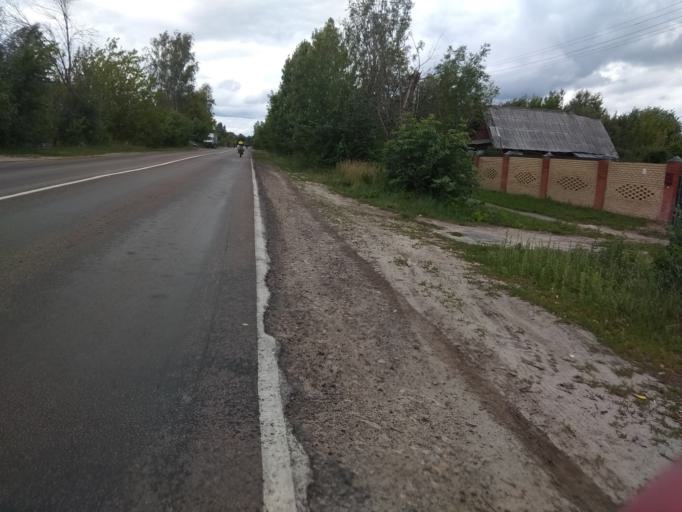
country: RU
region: Moskovskaya
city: Misheronskiy
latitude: 55.5970
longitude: 39.7036
